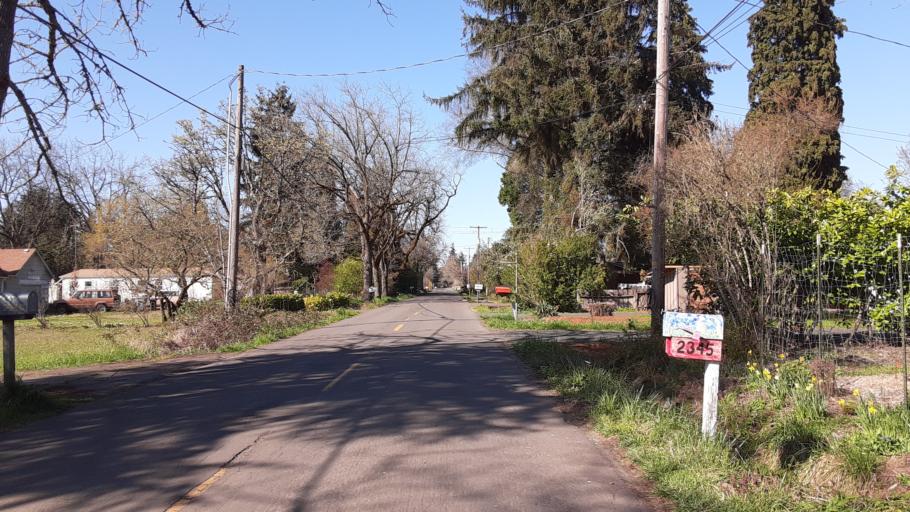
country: US
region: Oregon
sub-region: Benton County
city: Corvallis
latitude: 44.5425
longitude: -123.2556
